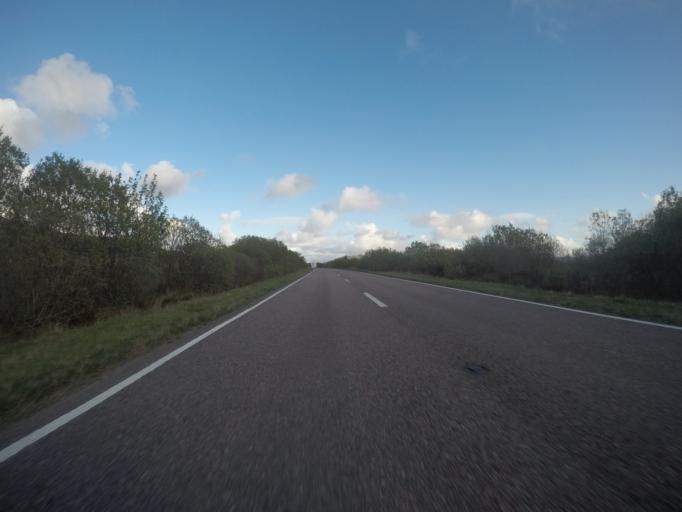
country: GB
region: Scotland
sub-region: Highland
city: Portree
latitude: 57.4610
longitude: -6.2806
